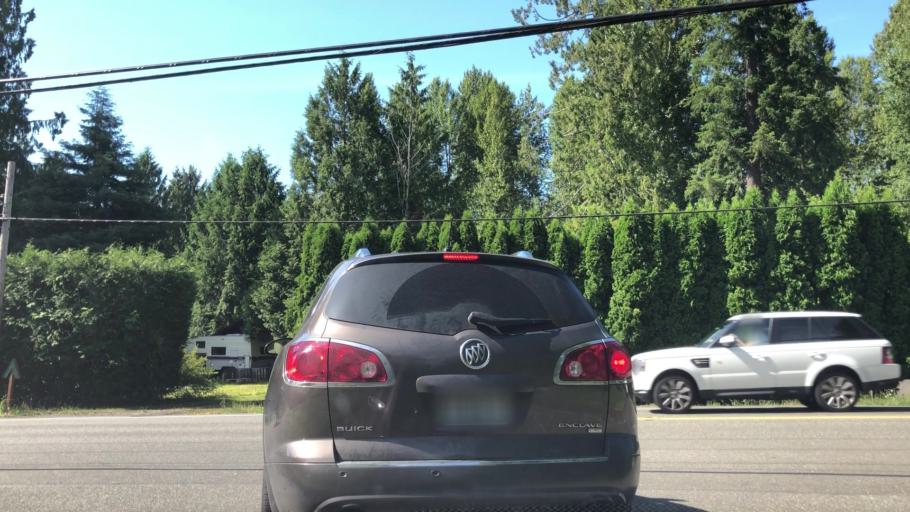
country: US
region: Washington
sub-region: King County
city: Cottage Lake
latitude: 47.7176
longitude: -122.0755
